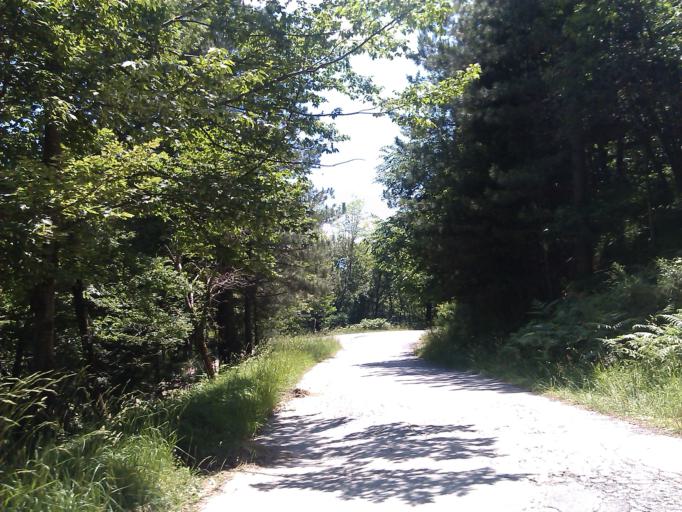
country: IT
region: Tuscany
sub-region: Provincia di Prato
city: Cantagallo
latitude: 43.9902
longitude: 11.0410
